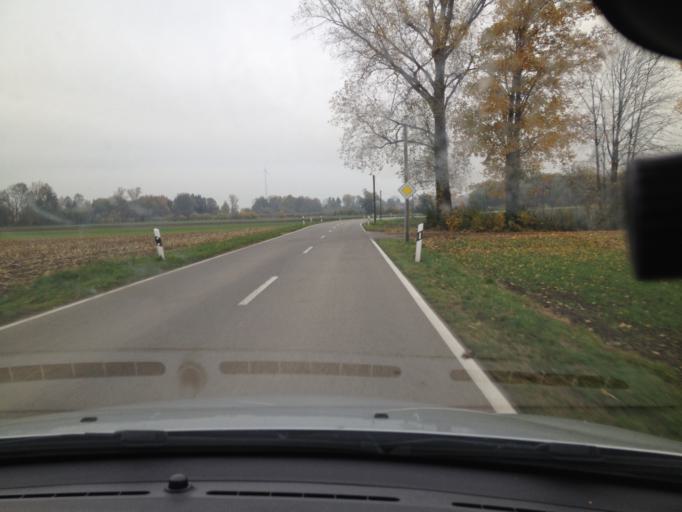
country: DE
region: Bavaria
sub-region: Swabia
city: Lamerdingen
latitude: 48.0968
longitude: 10.7263
